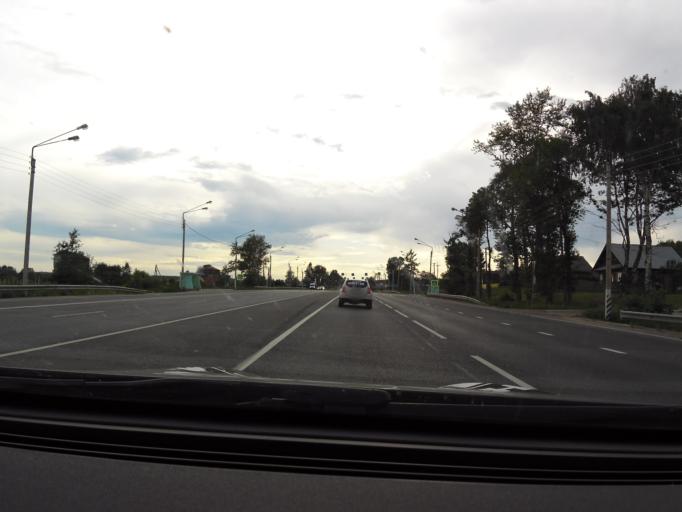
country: RU
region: Vladimir
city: Luknovo
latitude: 56.2393
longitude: 42.0737
